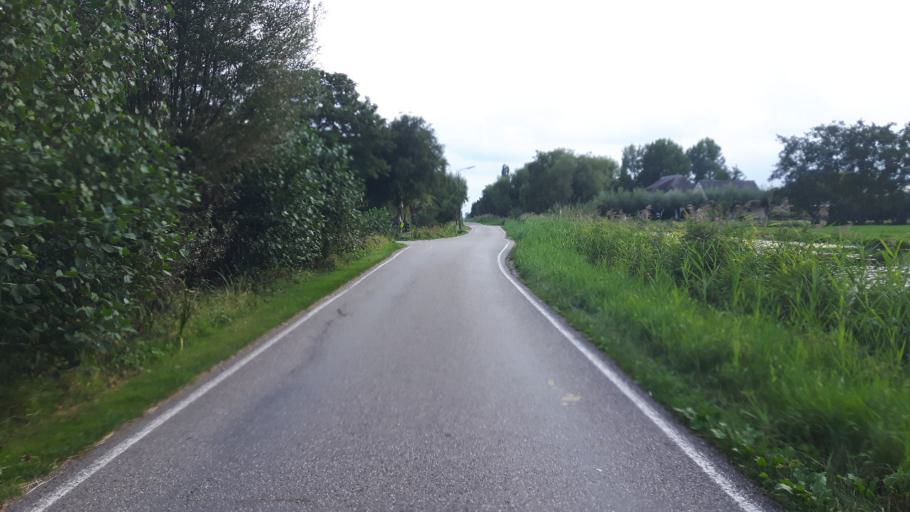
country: NL
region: Utrecht
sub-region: Gemeente De Ronde Venen
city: Mijdrecht
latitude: 52.1593
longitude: 4.8925
